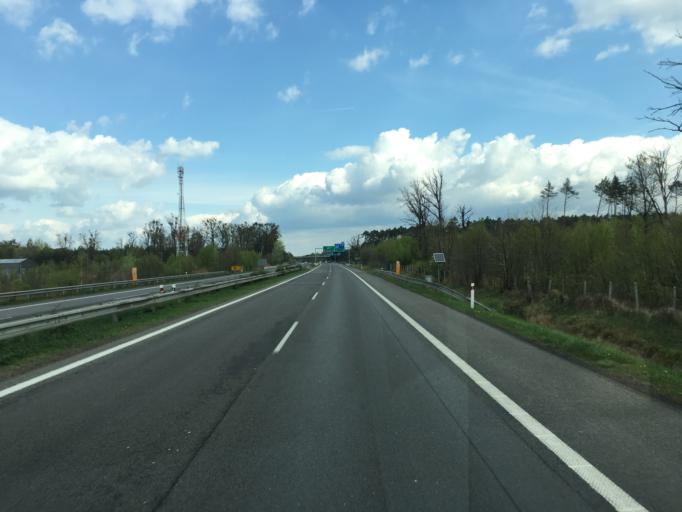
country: SK
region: Bratislavsky
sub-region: Okres Malacky
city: Malacky
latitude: 48.4218
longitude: 17.0408
